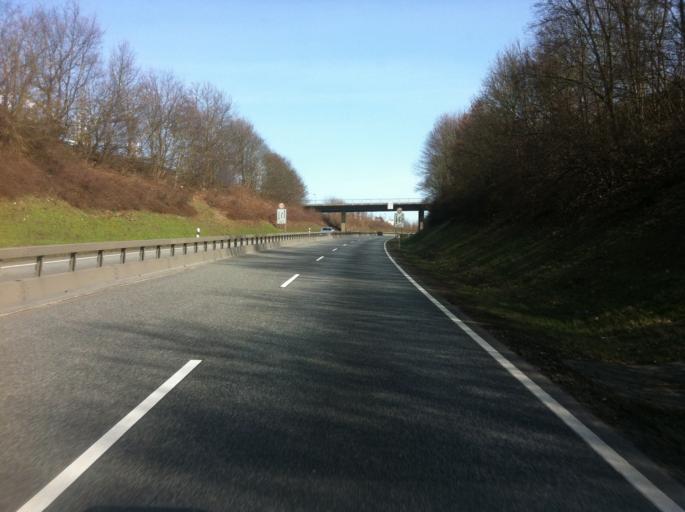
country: DE
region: Rheinland-Pfalz
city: Kottenheim
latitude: 50.3253
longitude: 7.2501
